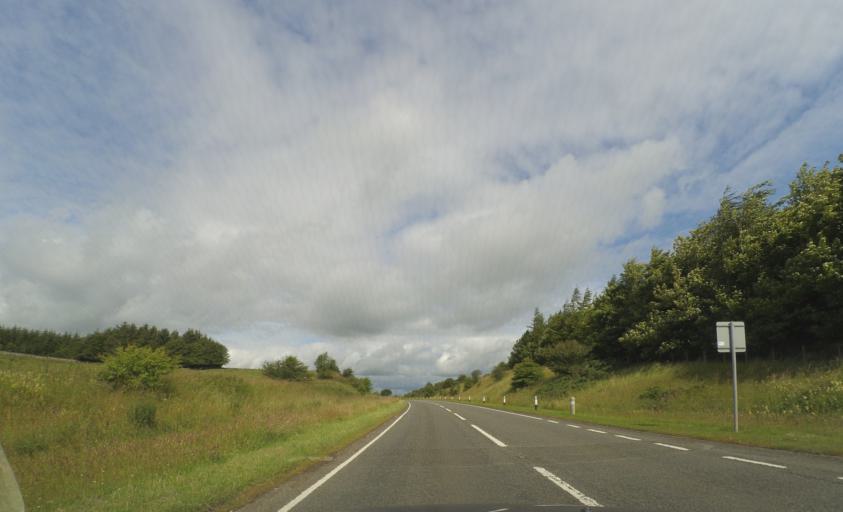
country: GB
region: Scotland
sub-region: The Scottish Borders
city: Hawick
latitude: 55.4711
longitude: -2.7940
